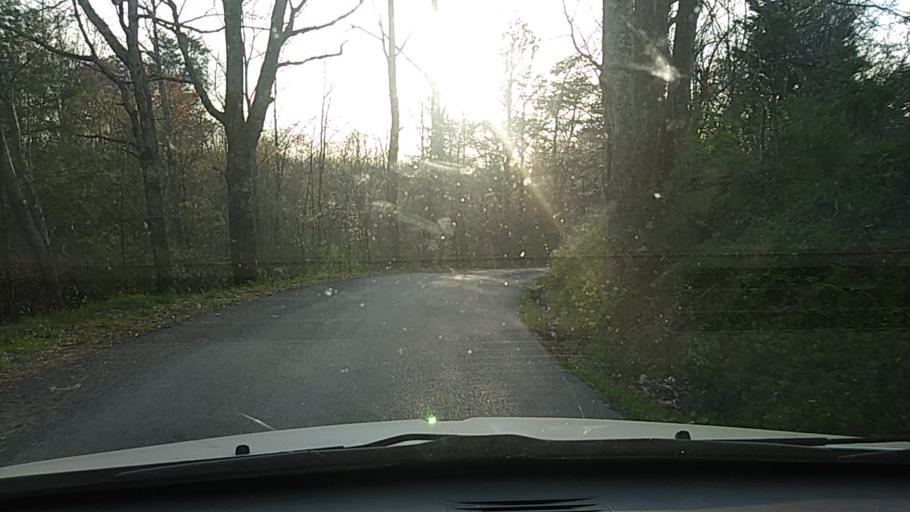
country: US
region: Tennessee
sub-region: Greene County
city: Tusculum
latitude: 36.0933
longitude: -82.7012
